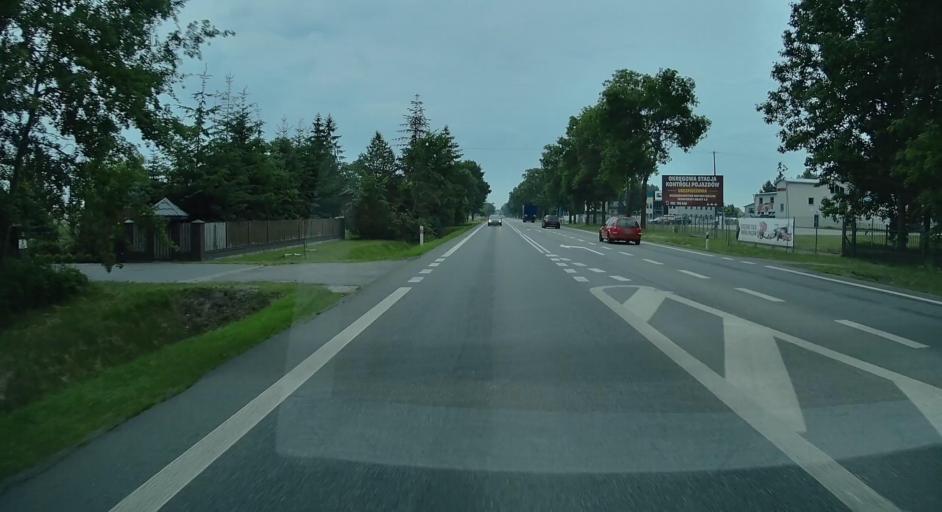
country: PL
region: Masovian Voivodeship
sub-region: Powiat siedlecki
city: Zbuczyn
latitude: 52.0972
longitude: 22.4131
